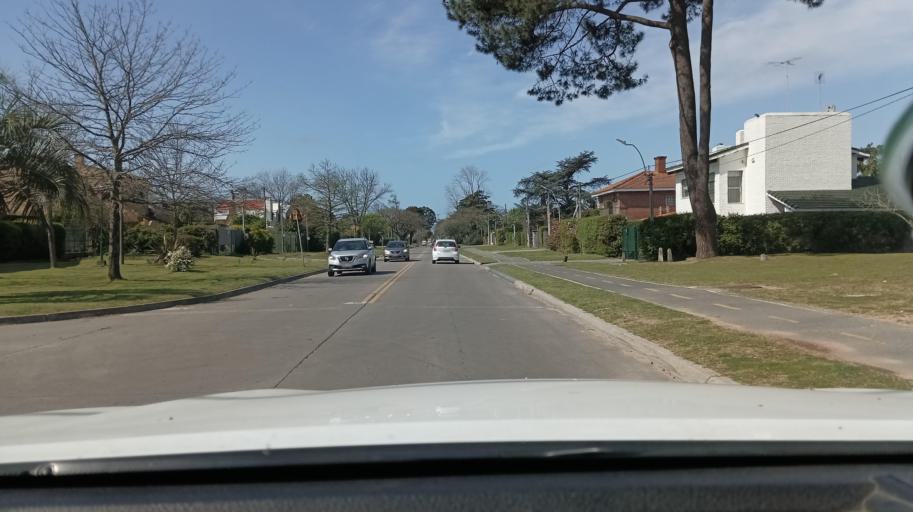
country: UY
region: Canelones
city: Paso de Carrasco
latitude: -34.8757
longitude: -56.0558
